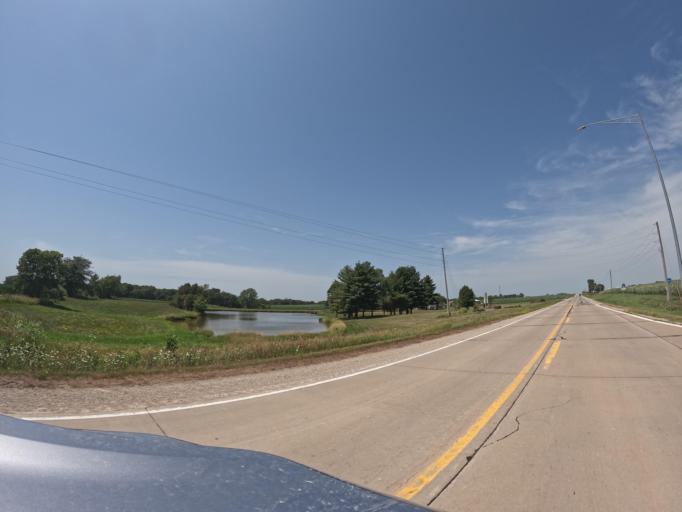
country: US
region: Iowa
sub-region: Henry County
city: Mount Pleasant
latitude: 40.9860
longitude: -91.6124
